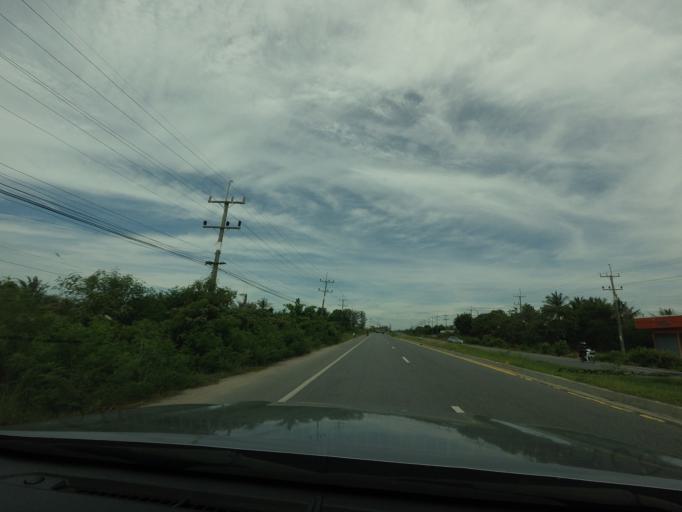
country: TH
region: Songkhla
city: Ranot
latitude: 7.8208
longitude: 100.3575
